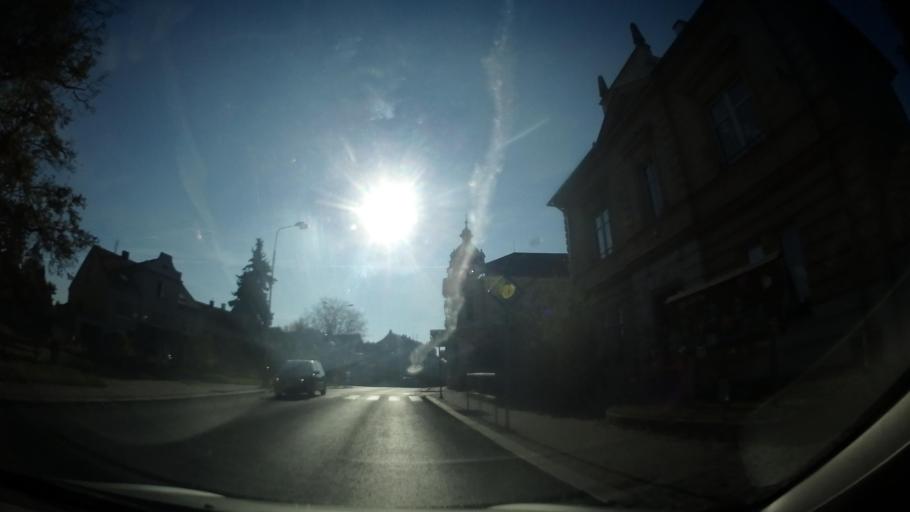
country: CZ
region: Central Bohemia
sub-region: Okres Praha-Vychod
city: Ricany
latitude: 49.9951
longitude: 14.6597
